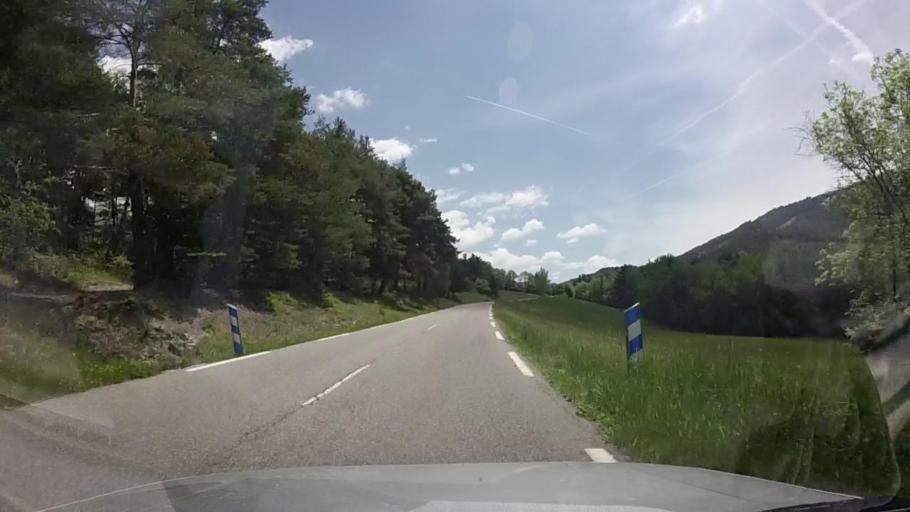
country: FR
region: Provence-Alpes-Cote d'Azur
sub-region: Departement des Alpes-de-Haute-Provence
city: Seyne-les-Alpes
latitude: 44.3369
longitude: 6.3853
